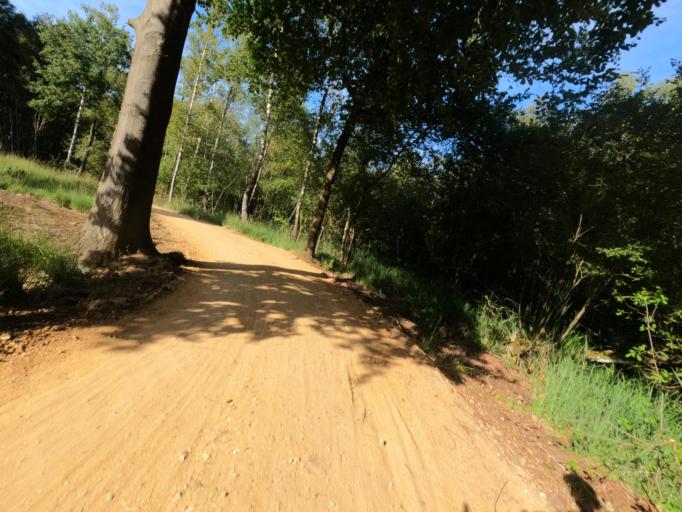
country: NL
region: Limburg
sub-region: Gemeente Beesel
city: Offenbeek
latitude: 51.2266
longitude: 6.0959
